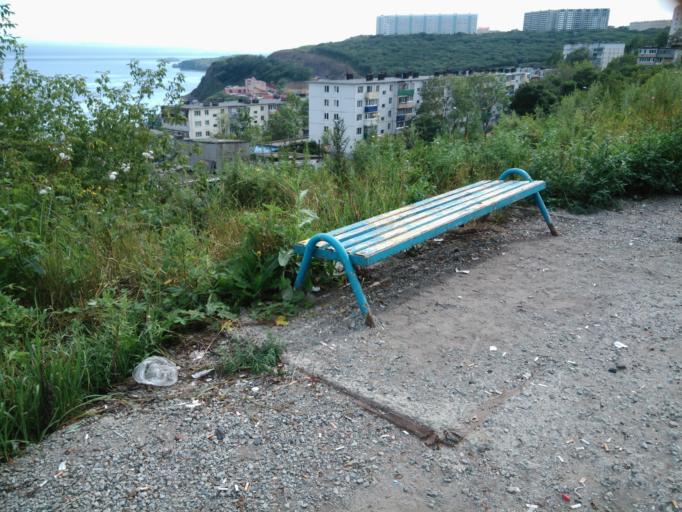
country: RU
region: Primorskiy
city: Vladivostok
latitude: 43.0923
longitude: 131.9749
